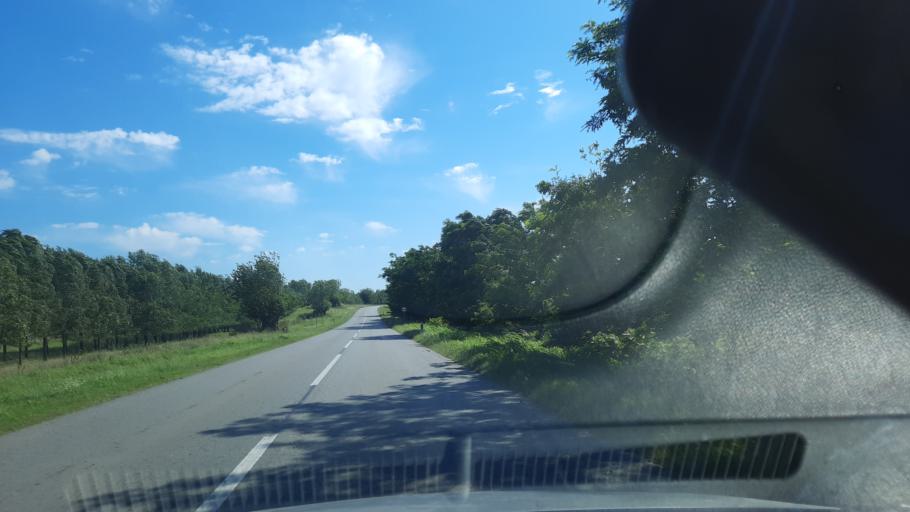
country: RO
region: Caras-Severin
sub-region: Comuna Socol
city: Socol
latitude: 44.8694
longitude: 21.3146
